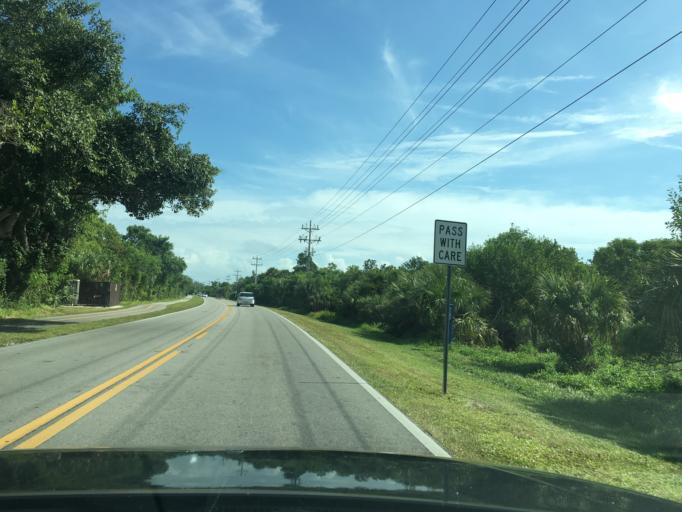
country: US
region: Florida
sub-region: Lee County
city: Saint James City
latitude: 26.4382
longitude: -82.0872
